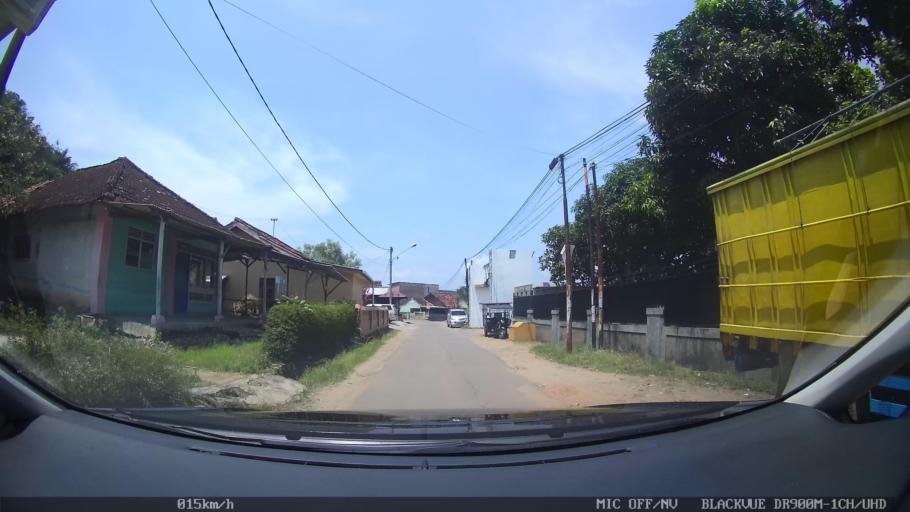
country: ID
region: Lampung
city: Kedaton
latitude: -5.3915
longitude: 105.2703
